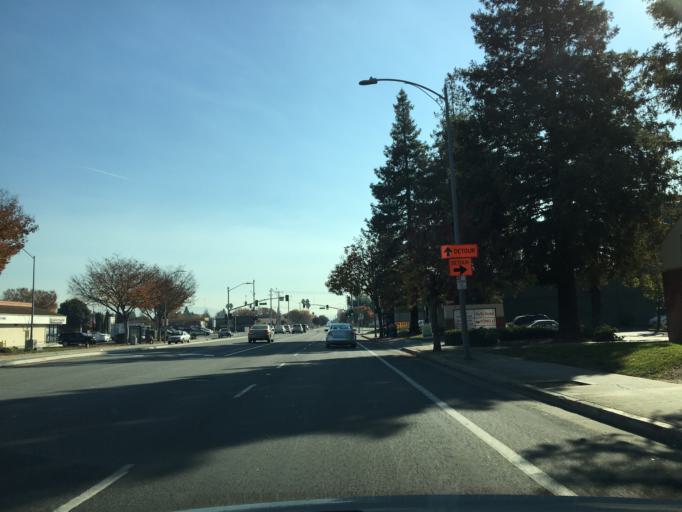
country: US
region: California
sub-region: Santa Clara County
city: Alum Rock
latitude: 37.3662
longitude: -121.8512
